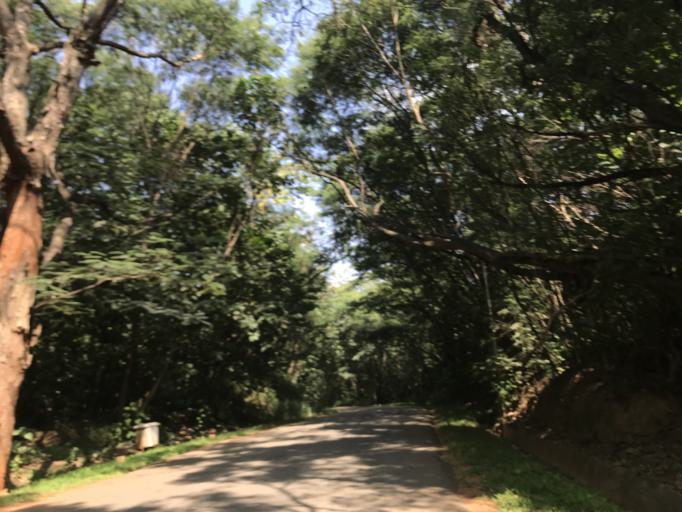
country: IN
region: Karnataka
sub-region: Bangalore Urban
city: Bangalore
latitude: 13.0254
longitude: 77.5688
